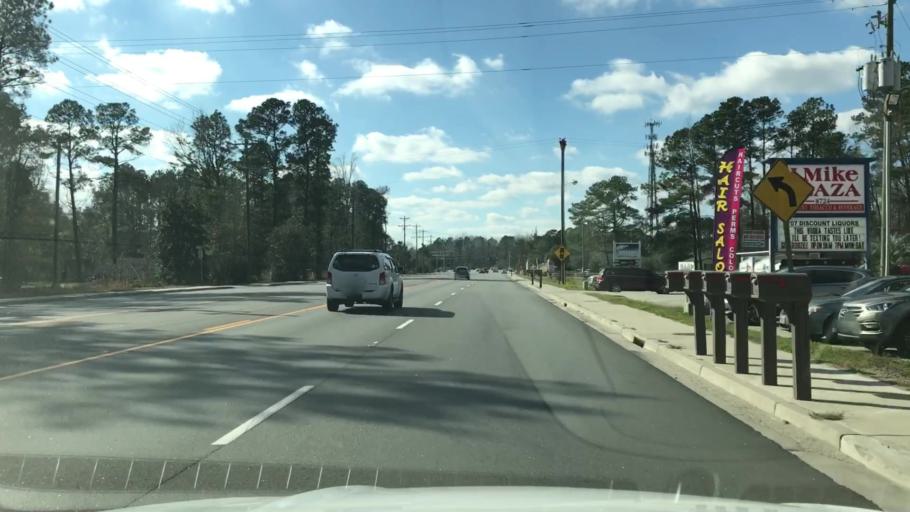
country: US
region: South Carolina
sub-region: Horry County
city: Socastee
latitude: 33.6418
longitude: -79.0296
